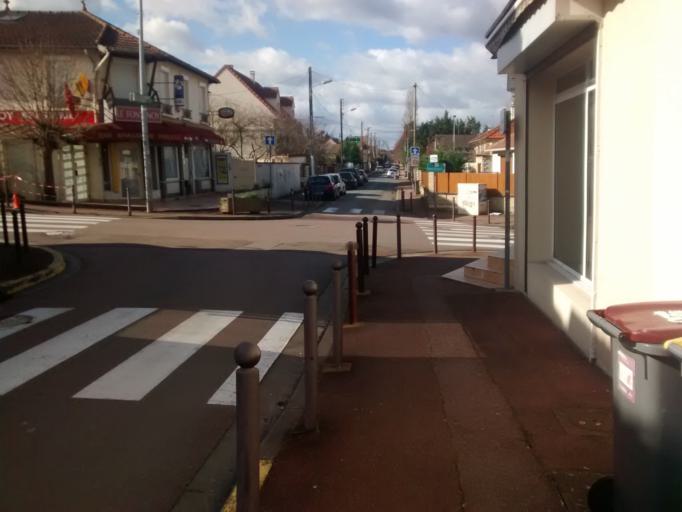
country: FR
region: Ile-de-France
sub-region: Departement de l'Essonne
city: Bures-sur-Yvette
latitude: 48.6943
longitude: 2.1532
